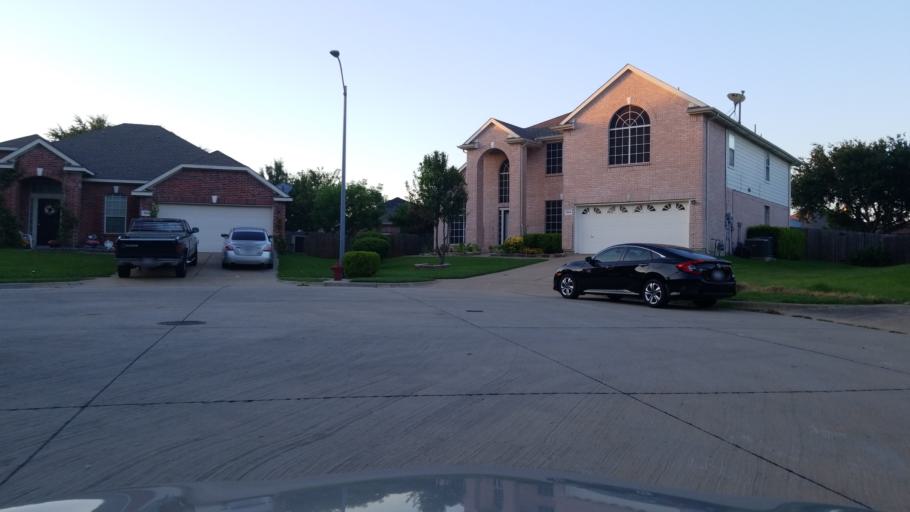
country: US
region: Texas
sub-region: Dallas County
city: Grand Prairie
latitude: 32.6856
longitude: -97.0387
